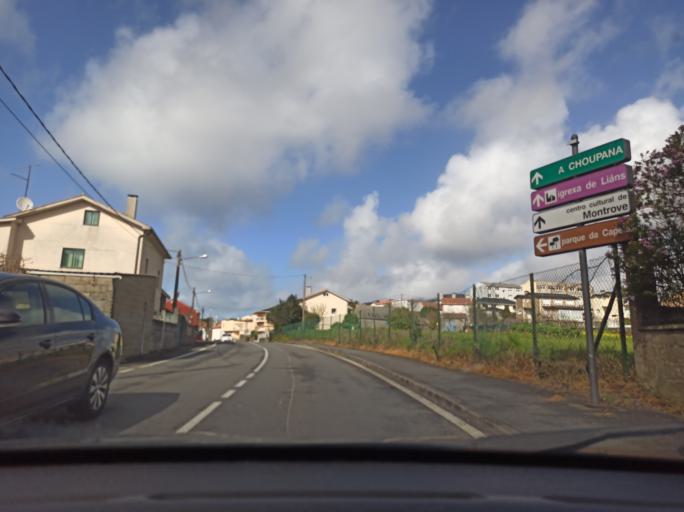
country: ES
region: Galicia
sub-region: Provincia da Coruna
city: Cambre
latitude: 43.3276
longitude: -8.3538
